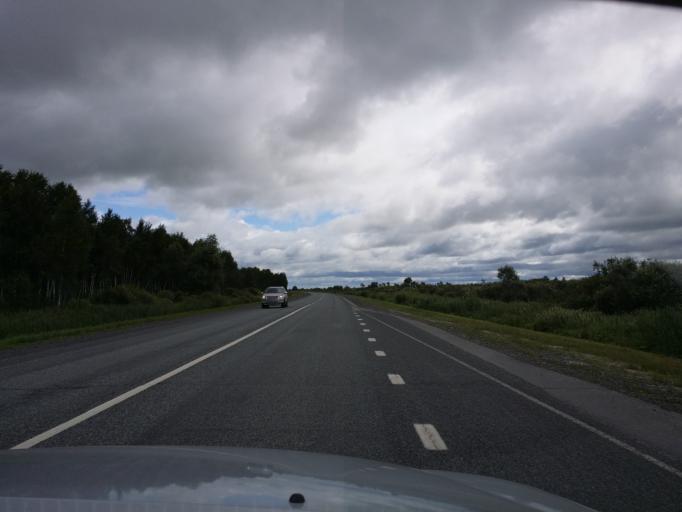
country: RU
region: Tjumen
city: Yarkovo
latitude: 57.2550
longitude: 66.8190
